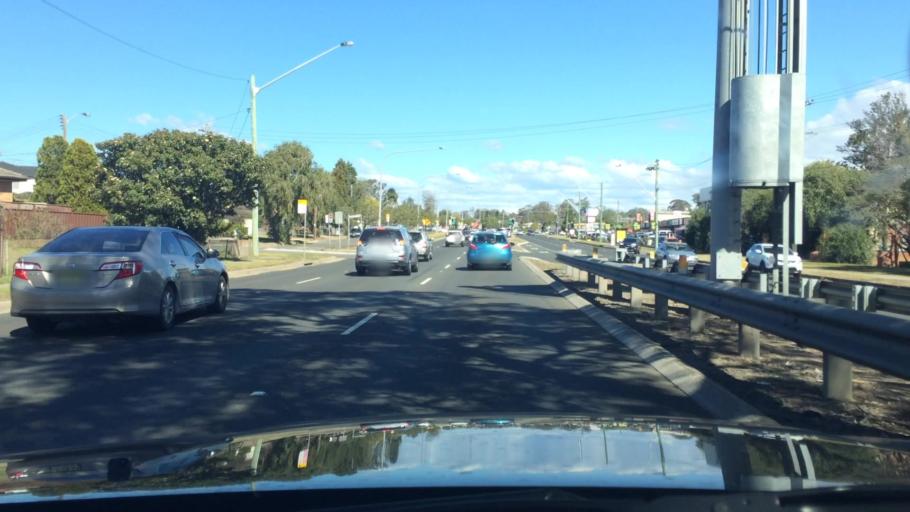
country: AU
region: New South Wales
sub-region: Campbelltown Municipality
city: Glenfield
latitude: -33.9418
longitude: 150.9119
